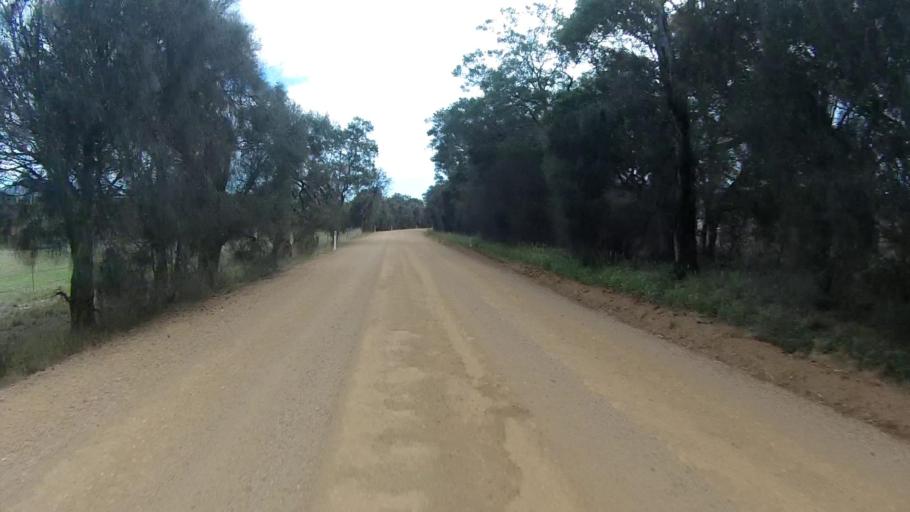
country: AU
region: Tasmania
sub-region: Sorell
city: Sorell
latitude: -42.7019
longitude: 147.4579
